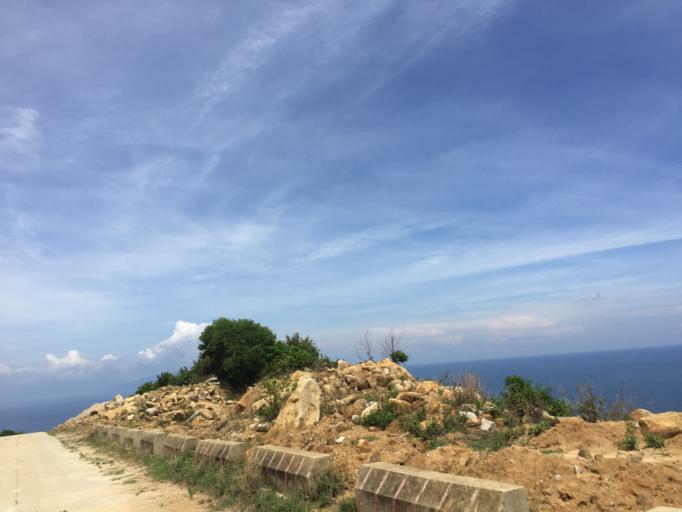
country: VN
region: Quang Nam
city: Hoi An
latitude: 15.9758
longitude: 108.5045
